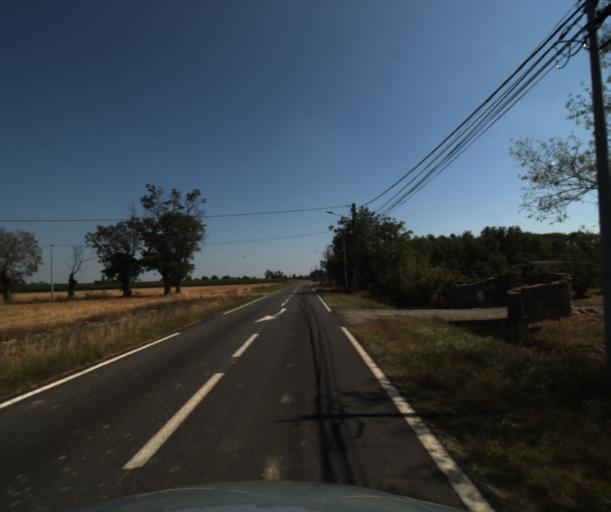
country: FR
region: Midi-Pyrenees
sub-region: Departement de la Haute-Garonne
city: Labastidette
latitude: 43.4684
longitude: 1.2523
